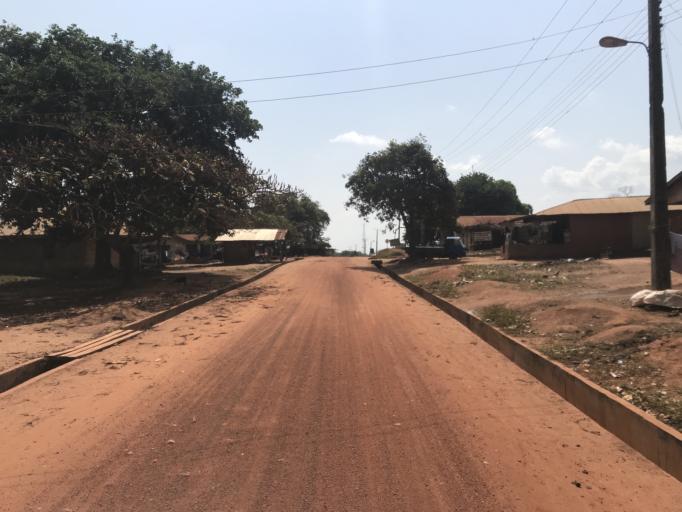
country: NG
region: Osun
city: Ifon
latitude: 7.8661
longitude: 4.4770
